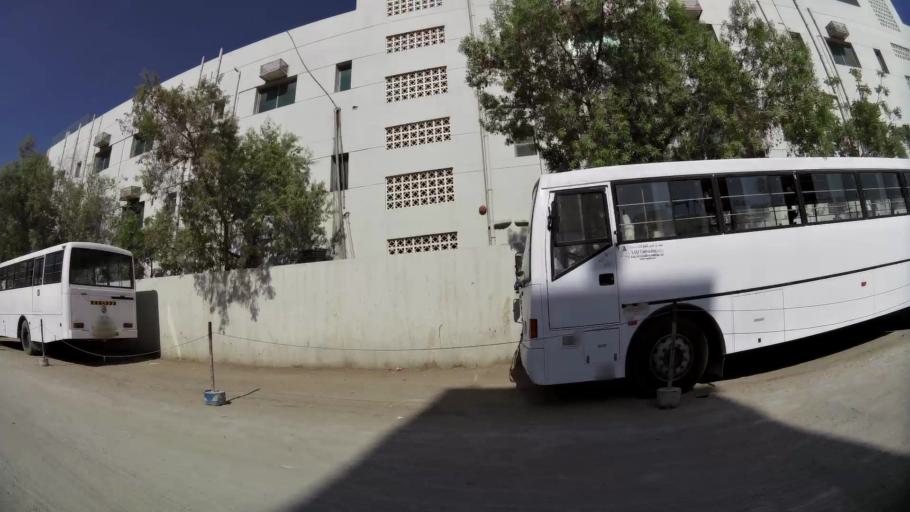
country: AE
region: Dubai
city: Dubai
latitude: 25.0080
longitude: 55.1070
